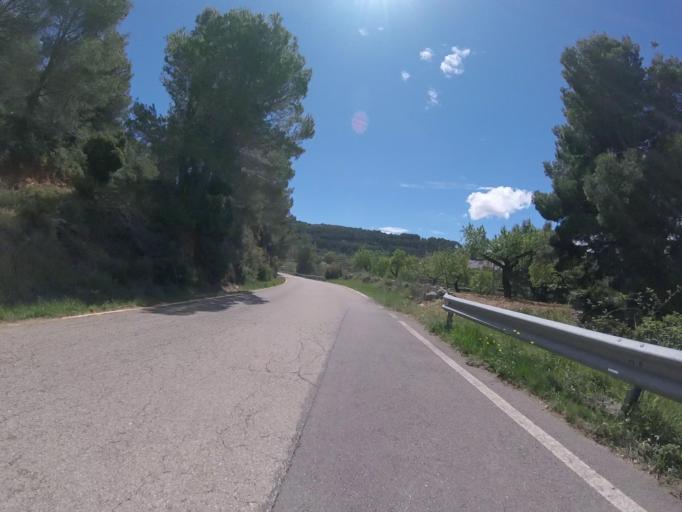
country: ES
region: Valencia
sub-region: Provincia de Castello
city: Sierra-Engarceran
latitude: 40.2739
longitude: -0.0200
